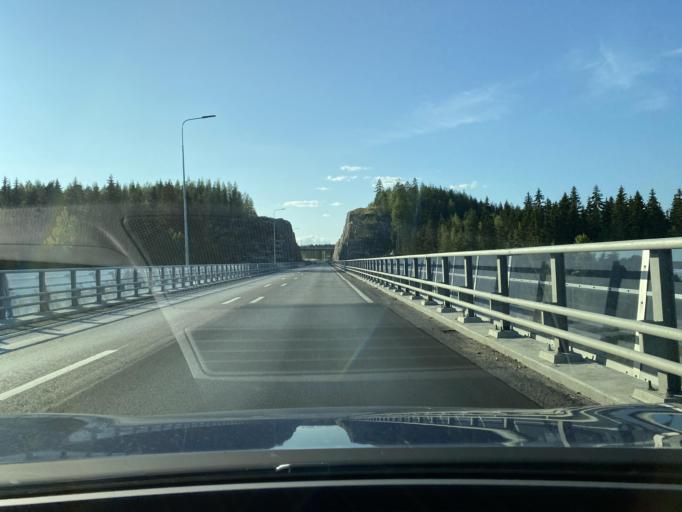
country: FI
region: Paijanne Tavastia
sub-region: Lahti
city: Hollola
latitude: 60.9554
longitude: 25.5649
